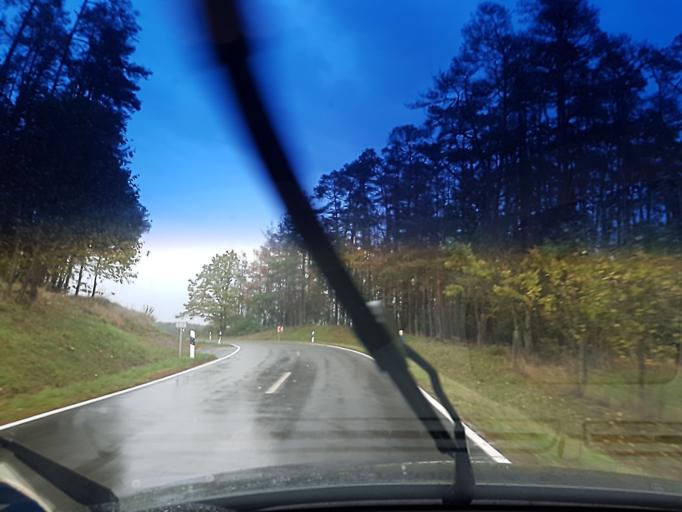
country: DE
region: Bavaria
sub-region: Regierungsbezirk Mittelfranken
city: Wachenroth
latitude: 49.7581
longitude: 10.6672
